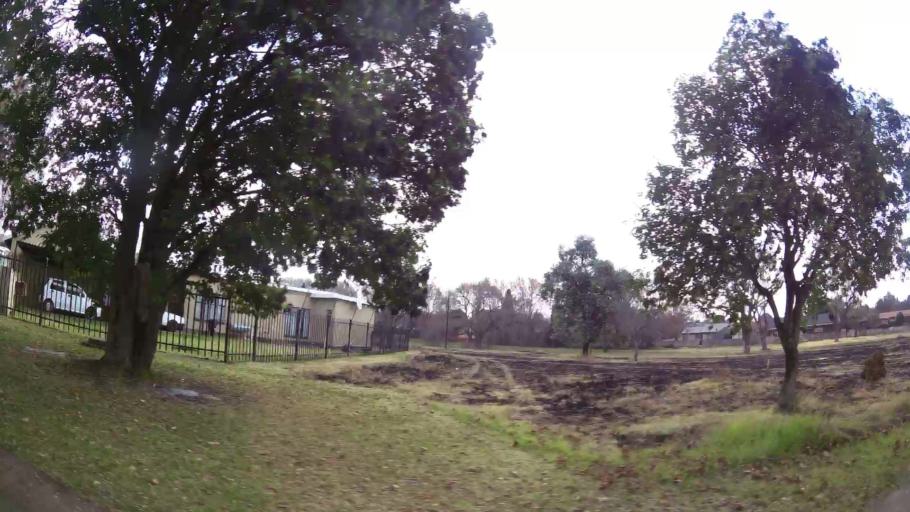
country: ZA
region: Mpumalanga
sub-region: Nkangala District Municipality
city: Delmas
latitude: -26.1438
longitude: 28.6743
